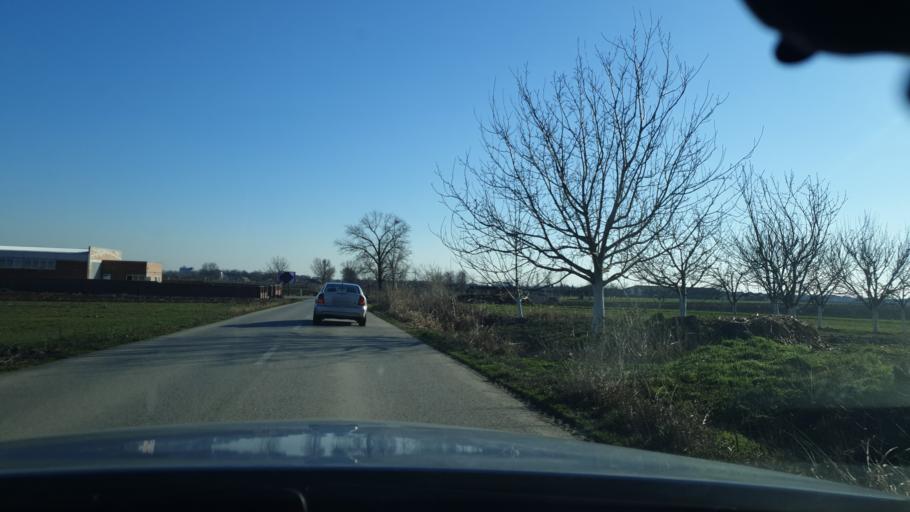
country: RS
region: Autonomna Pokrajina Vojvodina
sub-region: Sremski Okrug
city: Ruma
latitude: 45.0278
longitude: 19.8119
